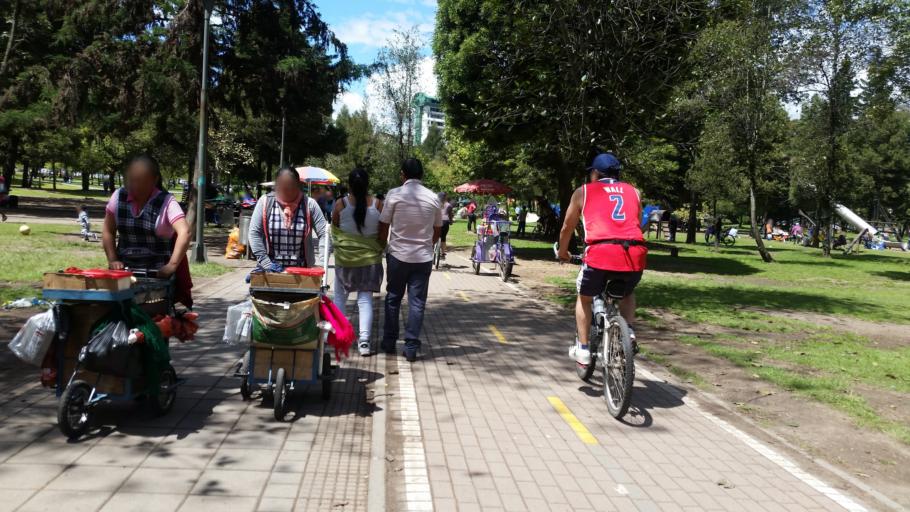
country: EC
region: Pichincha
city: Quito
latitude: -0.2089
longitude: -78.4990
